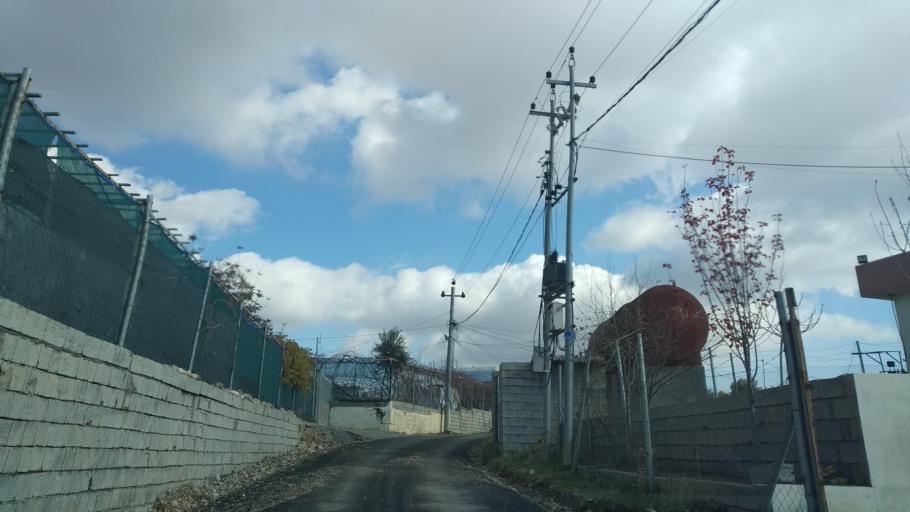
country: IQ
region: Arbil
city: Erbil
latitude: 36.2316
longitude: 44.1549
